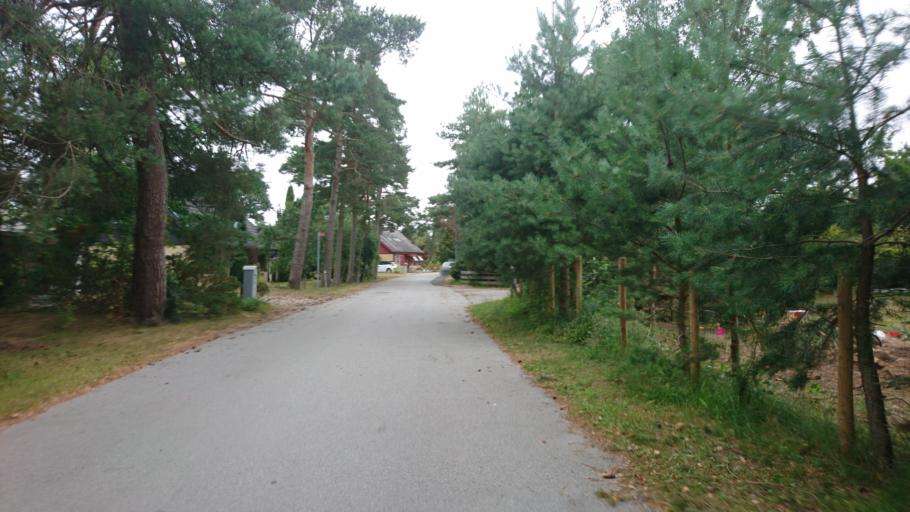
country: SE
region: Skane
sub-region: Vellinge Kommun
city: Ljunghusen
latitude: 55.3989
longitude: 12.9350
